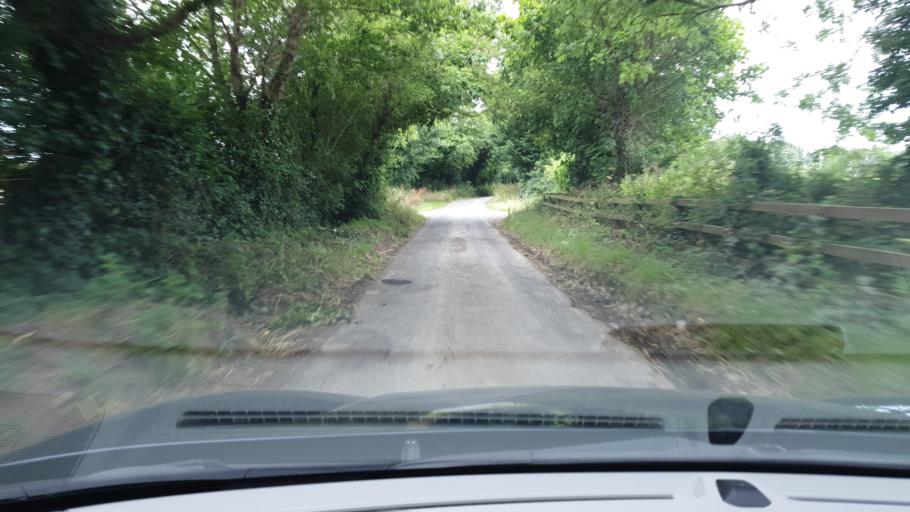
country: IE
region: Leinster
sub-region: An Mhi
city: Ashbourne
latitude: 53.5365
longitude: -6.3890
